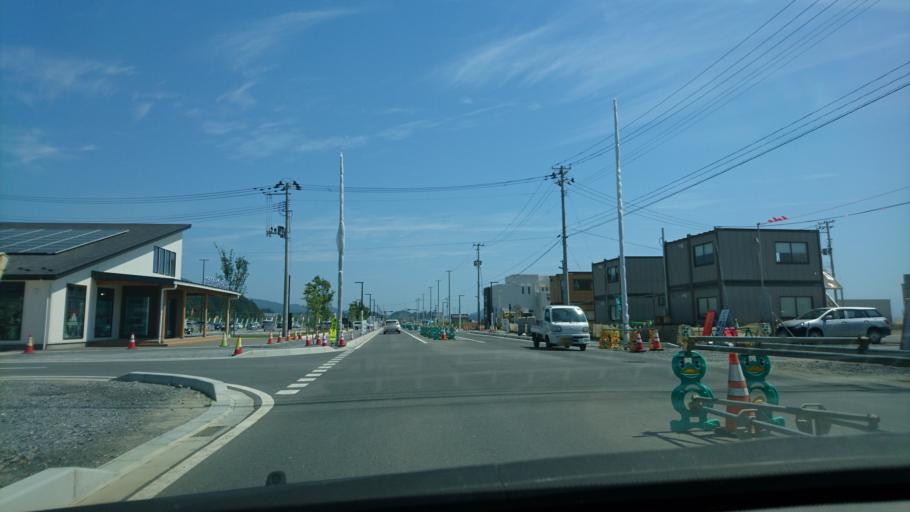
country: JP
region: Iwate
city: Ofunato
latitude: 39.0159
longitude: 141.6280
